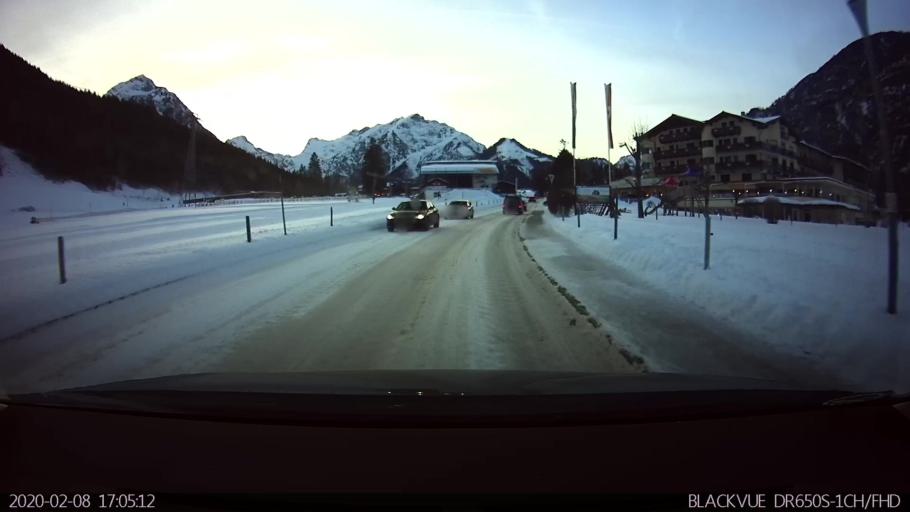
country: AT
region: Tyrol
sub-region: Politischer Bezirk Schwaz
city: Stans
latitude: 47.4370
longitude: 11.6990
